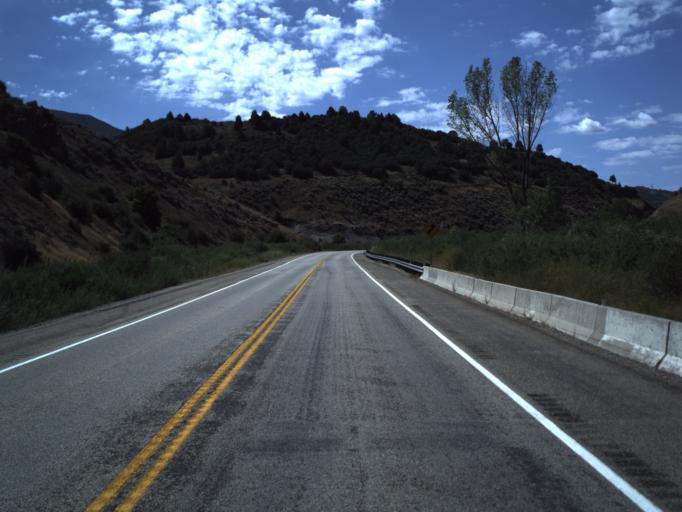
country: US
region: Utah
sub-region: Utah County
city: Woodland Hills
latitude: 39.9899
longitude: -111.4989
